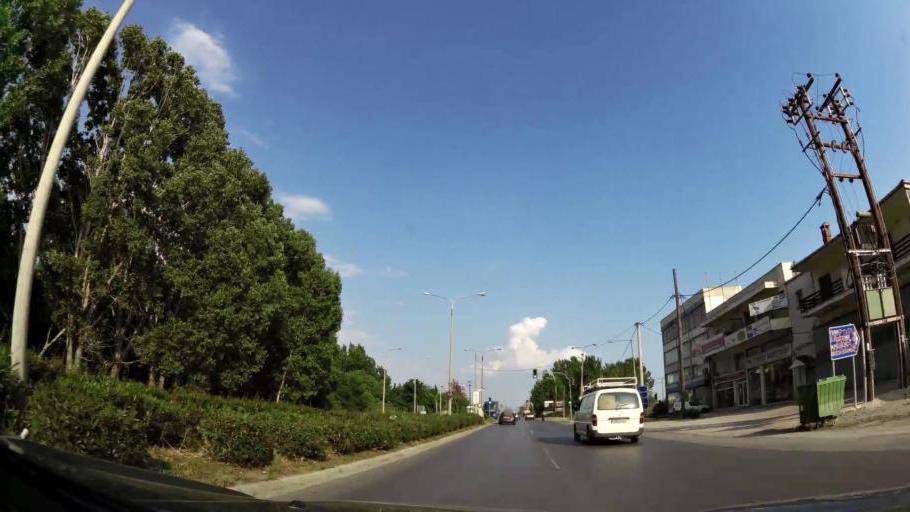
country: GR
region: Central Macedonia
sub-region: Nomos Thessalonikis
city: Diavata
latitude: 40.6801
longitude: 22.8666
